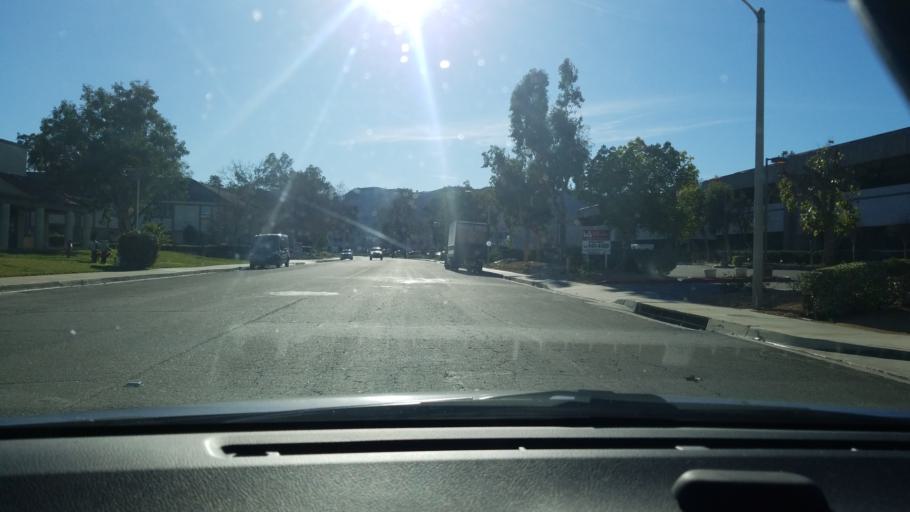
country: US
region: California
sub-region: Riverside County
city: Temecula
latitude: 33.5203
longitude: -117.1685
